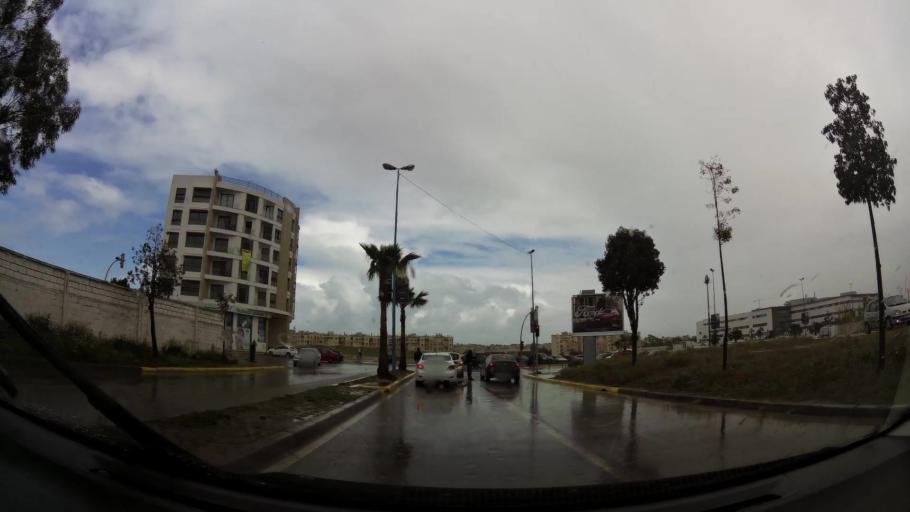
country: MA
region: Grand Casablanca
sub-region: Casablanca
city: Casablanca
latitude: 33.5502
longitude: -7.6702
